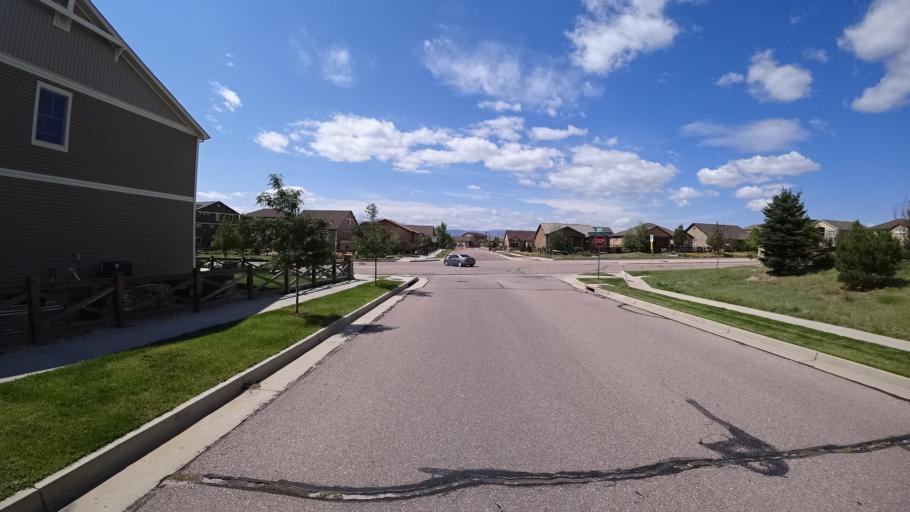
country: US
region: Colorado
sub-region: El Paso County
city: Cimarron Hills
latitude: 38.9279
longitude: -104.6773
